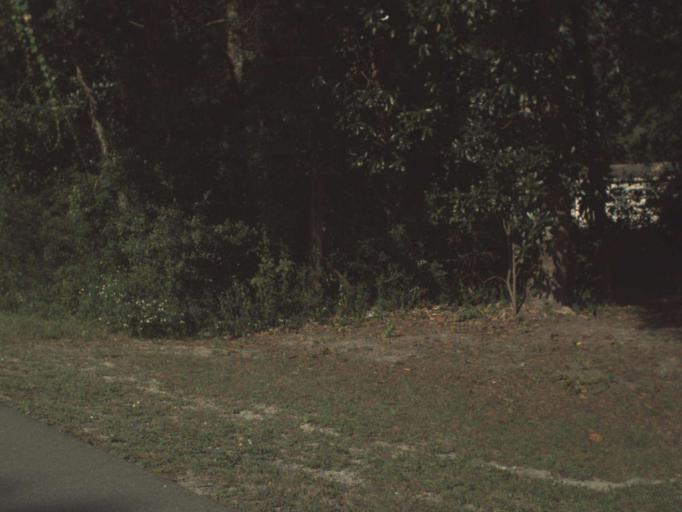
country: US
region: Florida
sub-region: Gulf County
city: Wewahitchka
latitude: 30.0645
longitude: -85.1916
